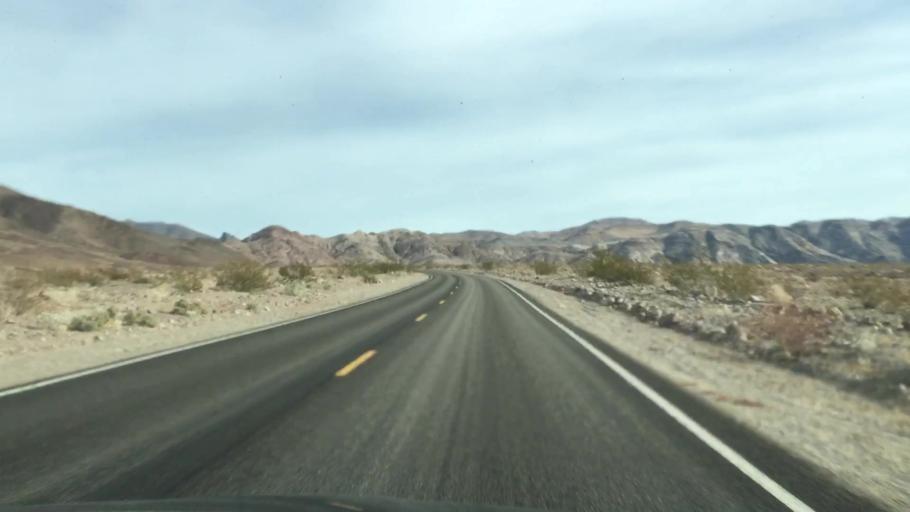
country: US
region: Nevada
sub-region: Nye County
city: Beatty
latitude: 36.7098
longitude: -116.9871
